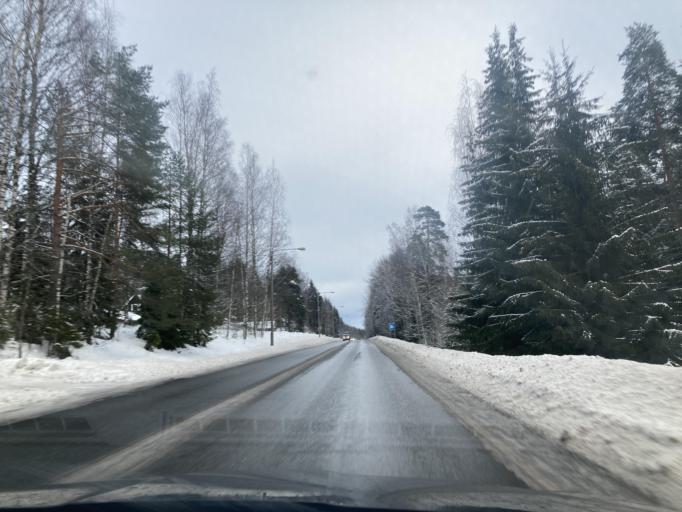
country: FI
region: Paijanne Tavastia
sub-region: Lahti
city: Asikkala
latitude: 61.1802
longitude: 25.5030
